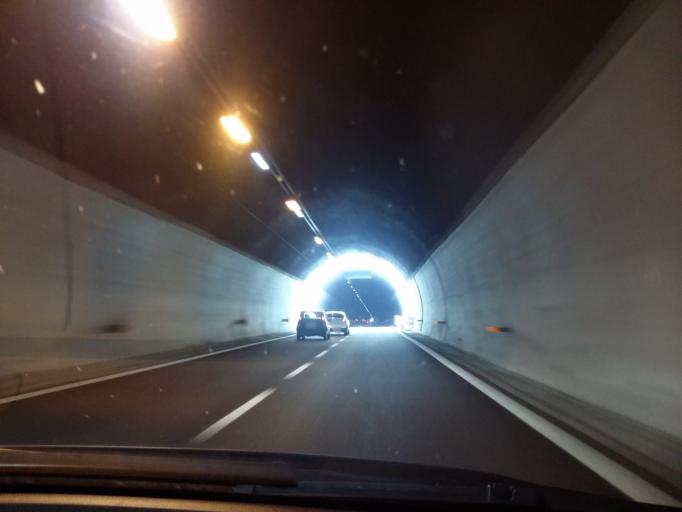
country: IT
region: Liguria
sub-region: Provincia di Savona
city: Albisola Marina
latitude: 44.3293
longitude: 8.4972
